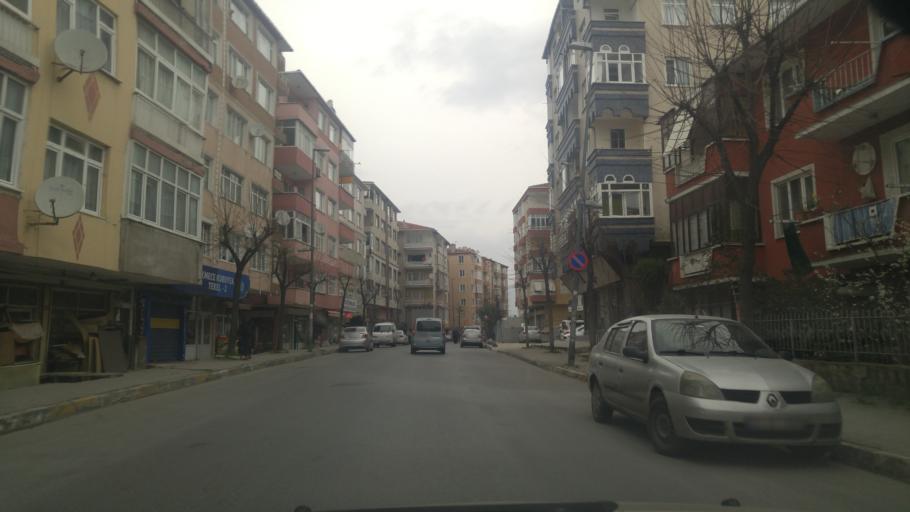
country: TR
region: Istanbul
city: Mahmutbey
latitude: 40.9976
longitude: 28.7662
